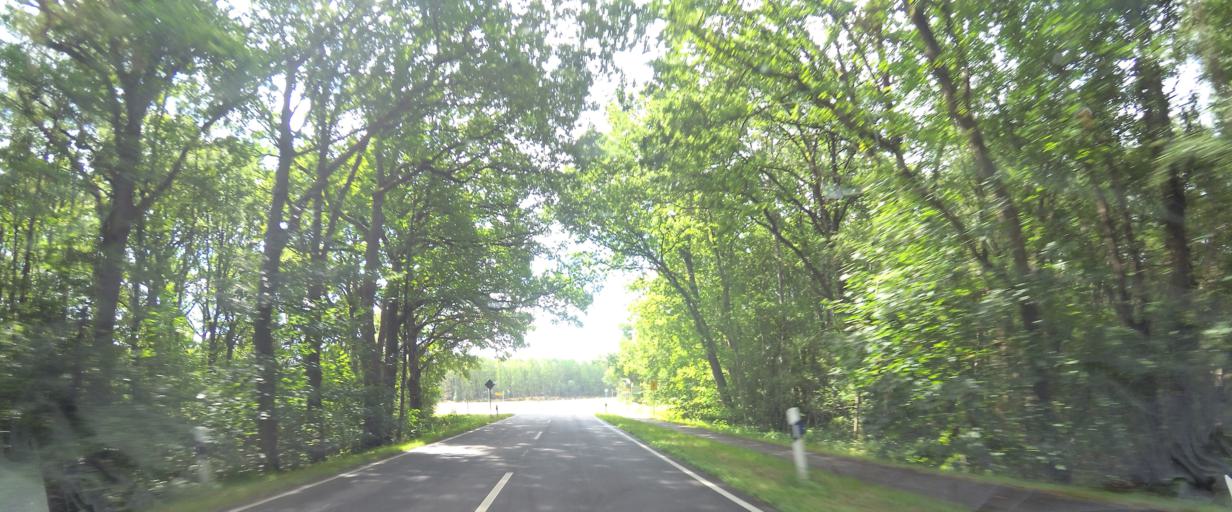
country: DE
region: Lower Saxony
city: Lathen
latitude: 52.8322
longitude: 7.3189
